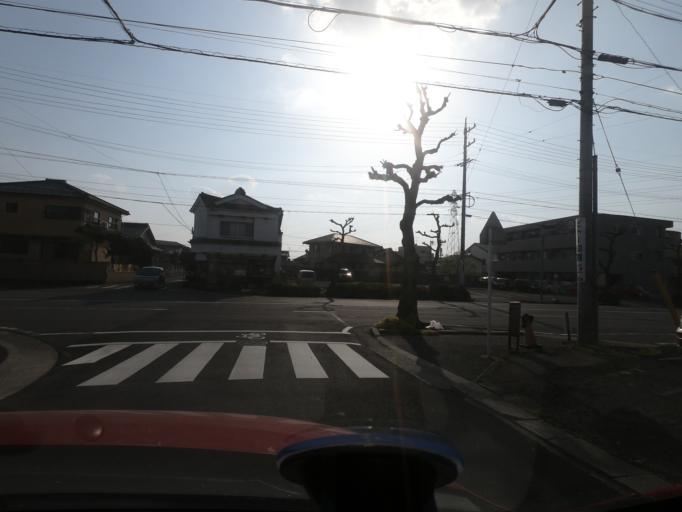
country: JP
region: Aichi
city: Kasugai
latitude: 35.2556
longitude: 136.9771
